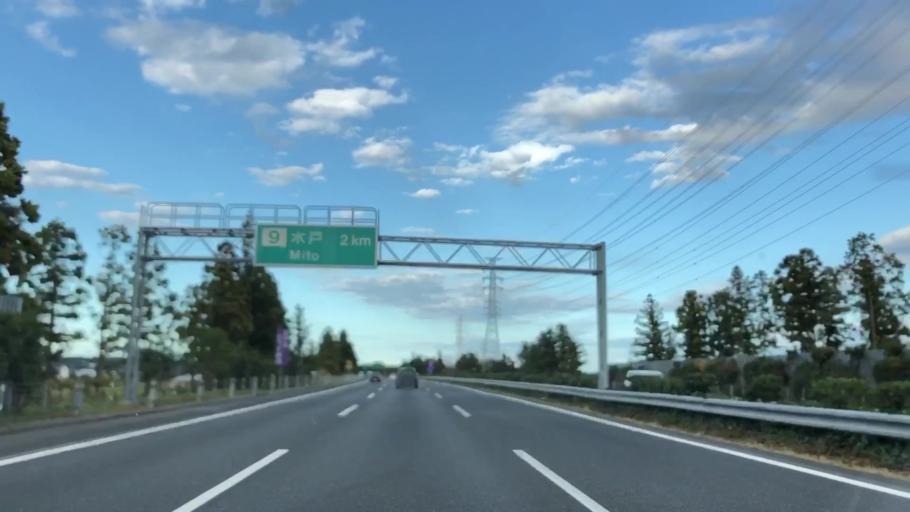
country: JP
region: Ibaraki
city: Mito-shi
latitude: 36.3644
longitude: 140.3795
